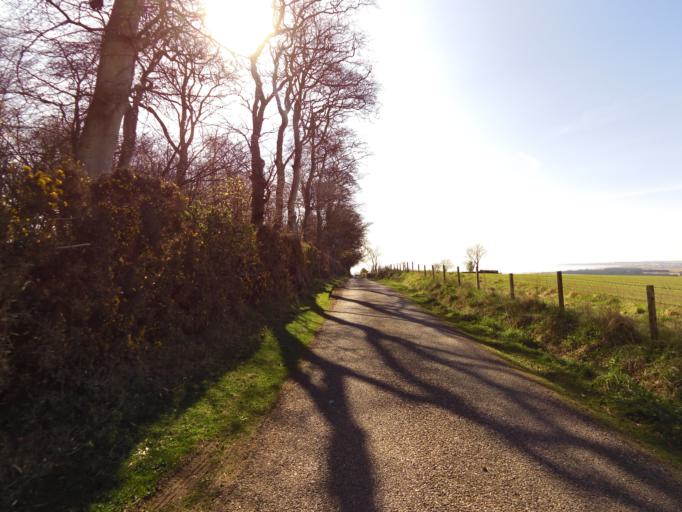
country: GB
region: Scotland
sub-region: Angus
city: Montrose
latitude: 56.7657
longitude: -2.4318
